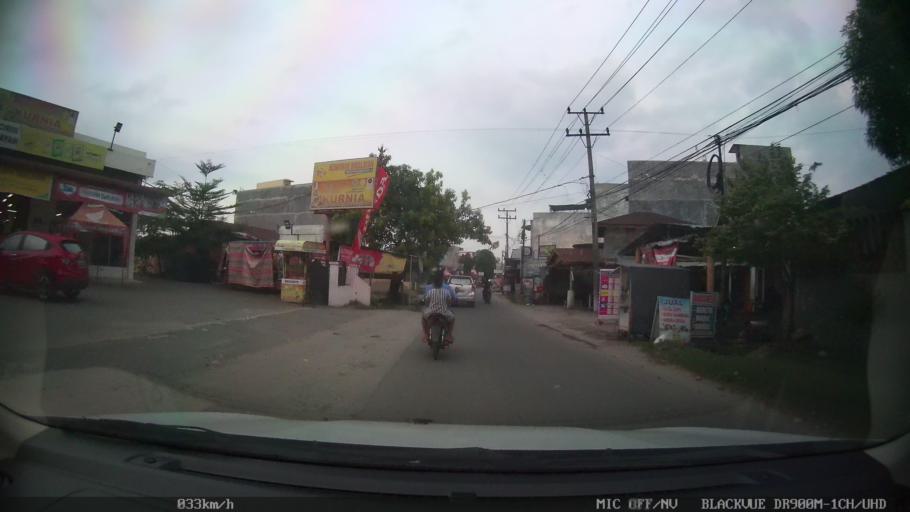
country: ID
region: North Sumatra
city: Sunggal
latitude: 3.5865
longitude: 98.5979
